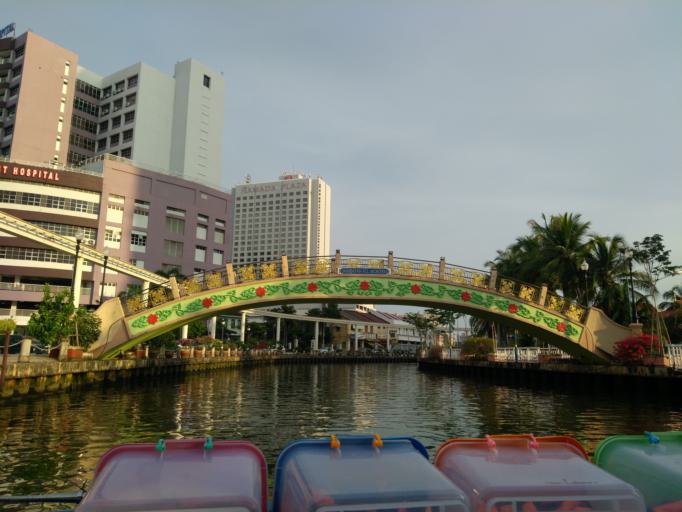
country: MY
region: Melaka
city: Malacca
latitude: 2.2032
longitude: 102.2517
